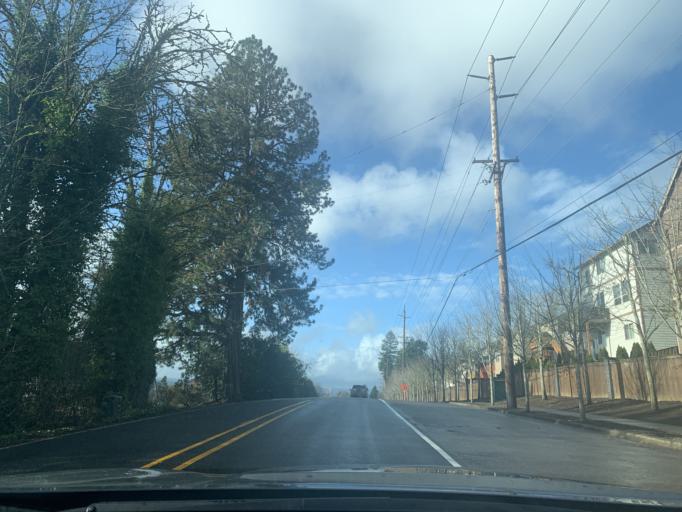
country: US
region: Oregon
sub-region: Washington County
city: King City
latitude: 45.4019
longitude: -122.8279
